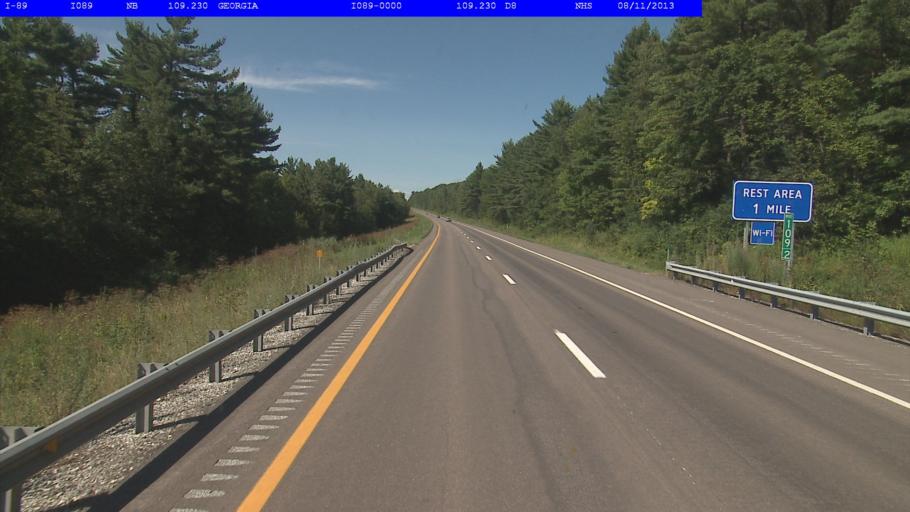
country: US
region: Vermont
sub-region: Franklin County
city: Saint Albans
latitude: 44.7301
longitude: -73.0801
